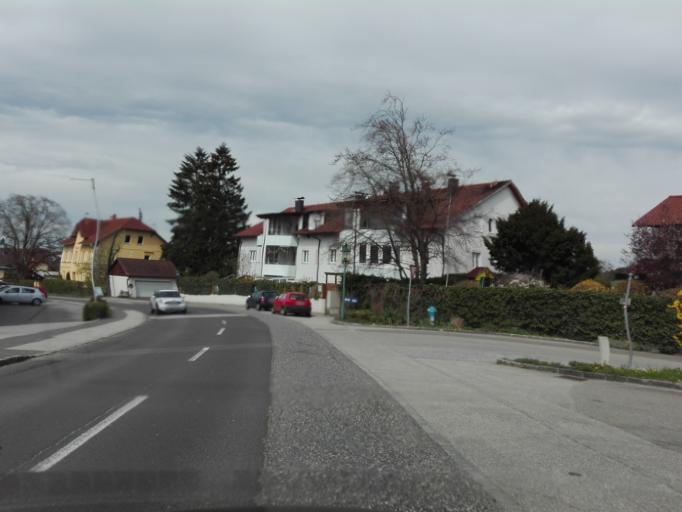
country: AT
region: Upper Austria
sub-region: Politischer Bezirk Urfahr-Umgebung
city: Gramastetten
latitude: 48.3807
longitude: 14.1950
